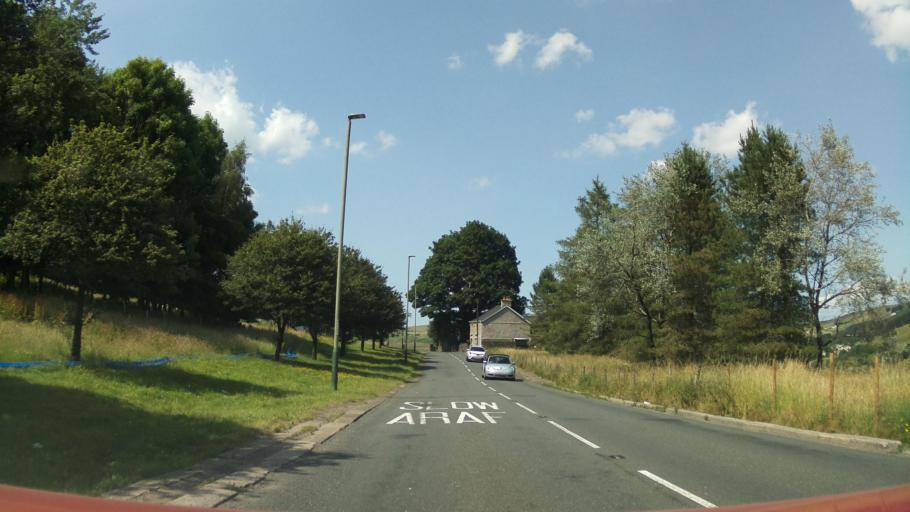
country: GB
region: Wales
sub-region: Caerphilly County Borough
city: New Tredegar
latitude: 51.7315
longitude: -3.2602
